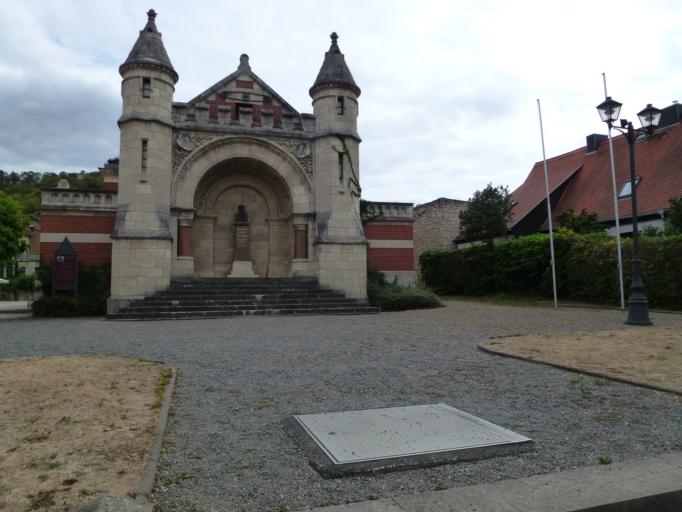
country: DE
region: Saxony-Anhalt
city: Freyburg
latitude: 51.2133
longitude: 11.7686
